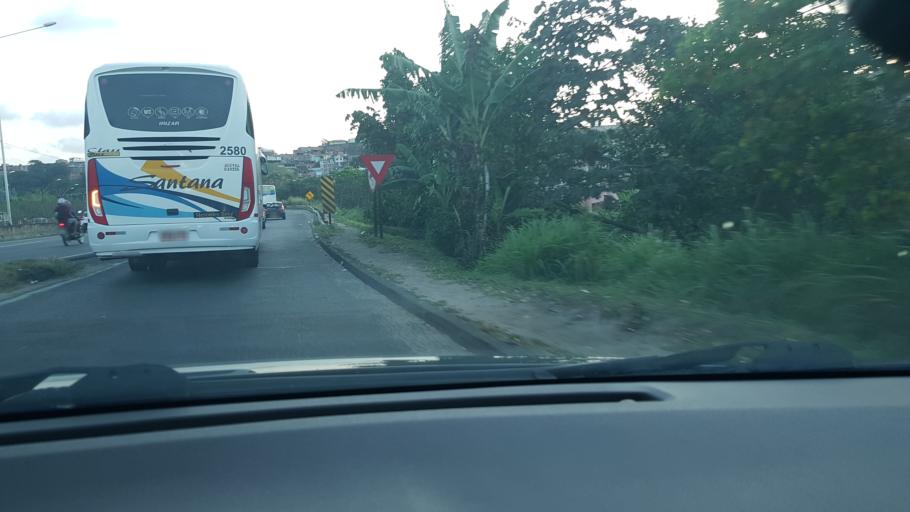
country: BR
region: Bahia
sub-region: Salvador
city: Salvador
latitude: -12.9297
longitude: -38.4698
